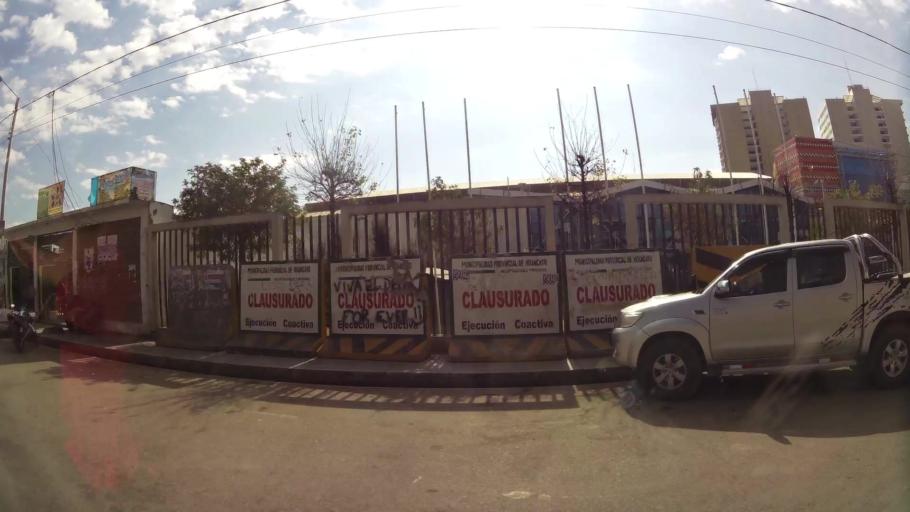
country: PE
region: Junin
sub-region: Provincia de Huancayo
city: El Tambo
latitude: -12.0750
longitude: -75.2141
